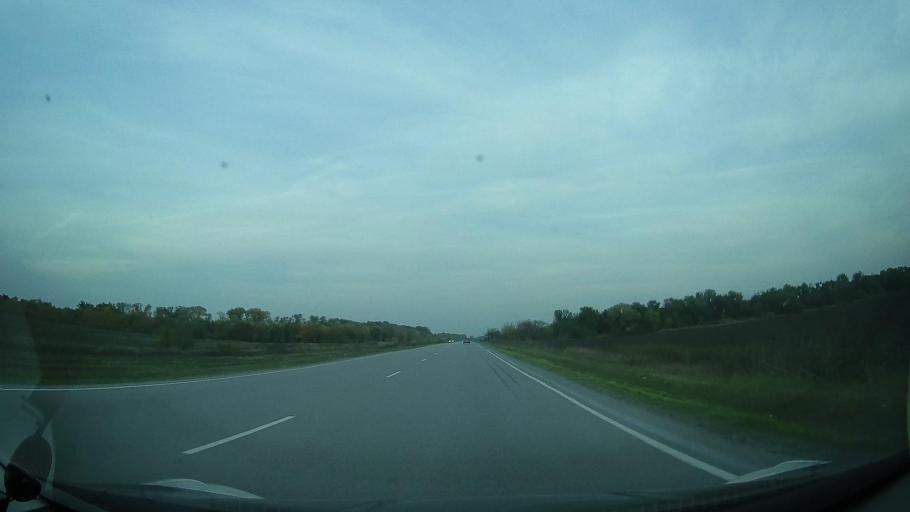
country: RU
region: Rostov
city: Ol'ginskaya
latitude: 47.1305
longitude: 39.9265
